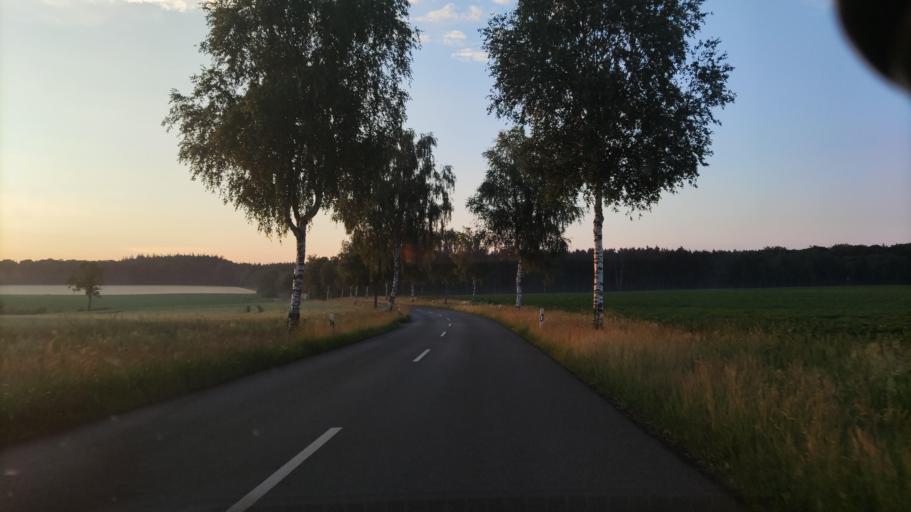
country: DE
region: Lower Saxony
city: Bispingen
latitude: 53.1158
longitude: 10.0574
